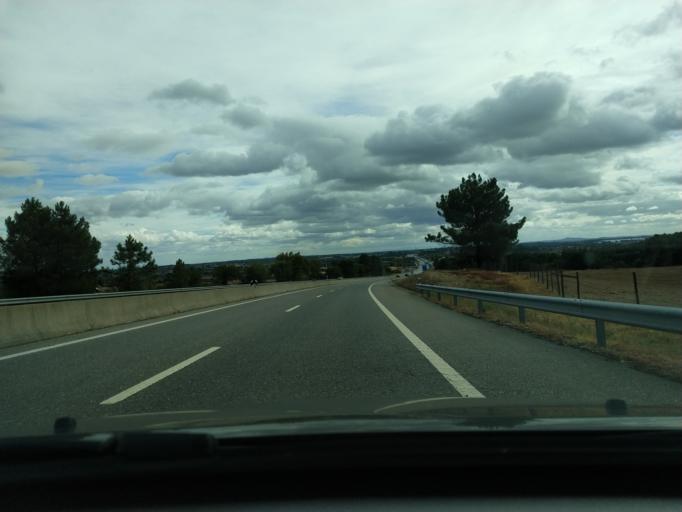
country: PT
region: Castelo Branco
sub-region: Concelho do Fundao
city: Fundao
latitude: 40.0435
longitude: -7.4706
